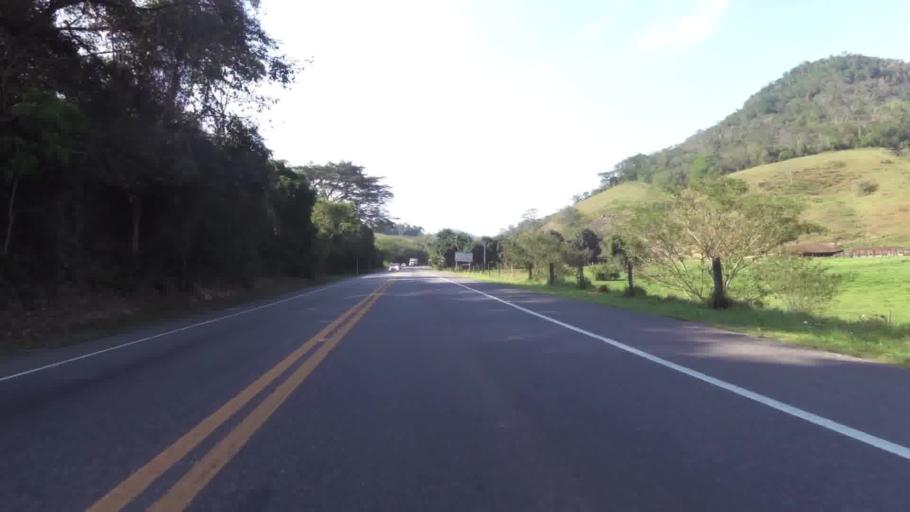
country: BR
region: Espirito Santo
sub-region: Rio Novo Do Sul
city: Rio Novo do Sul
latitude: -20.8526
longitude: -40.8778
